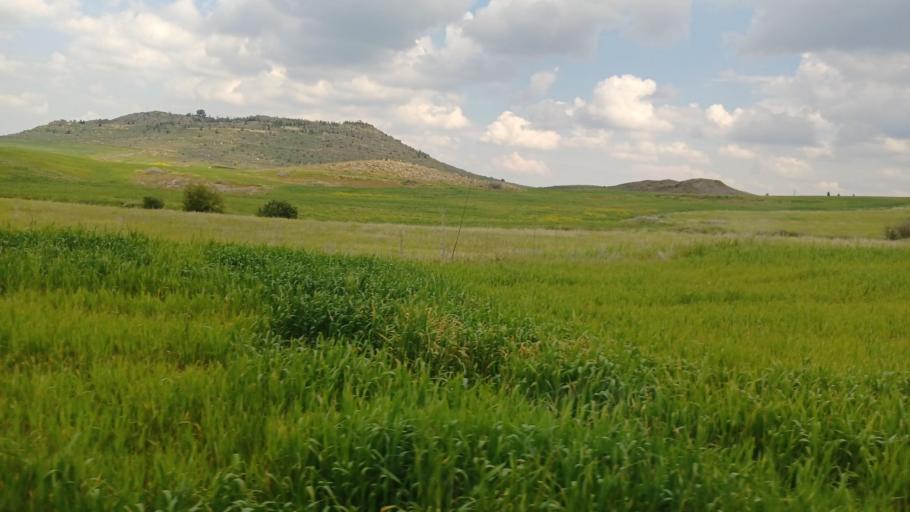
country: CY
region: Lefkosia
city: Lefka
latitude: 35.0846
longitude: 32.9484
